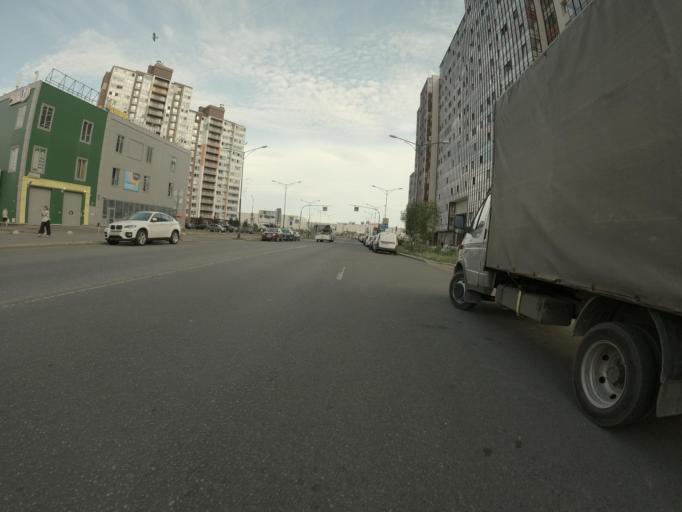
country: RU
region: Leningrad
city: Rybatskoye
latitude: 59.8984
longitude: 30.5119
